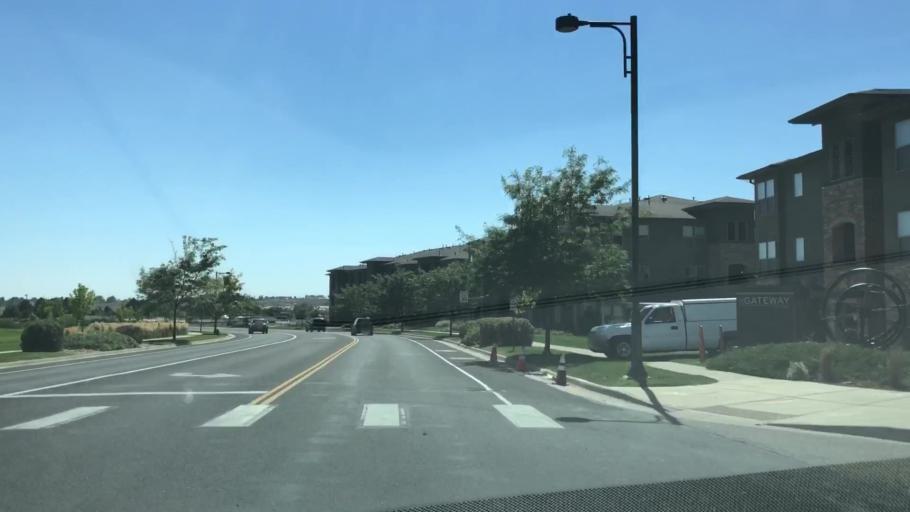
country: US
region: Colorado
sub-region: Larimer County
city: Loveland
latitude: 40.4035
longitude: -104.9834
